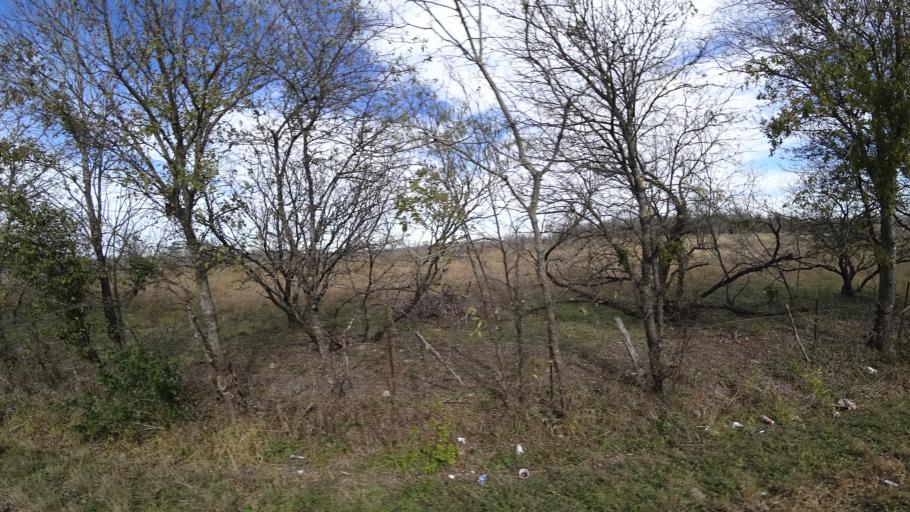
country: US
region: Texas
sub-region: Travis County
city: Onion Creek
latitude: 30.1193
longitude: -97.7306
